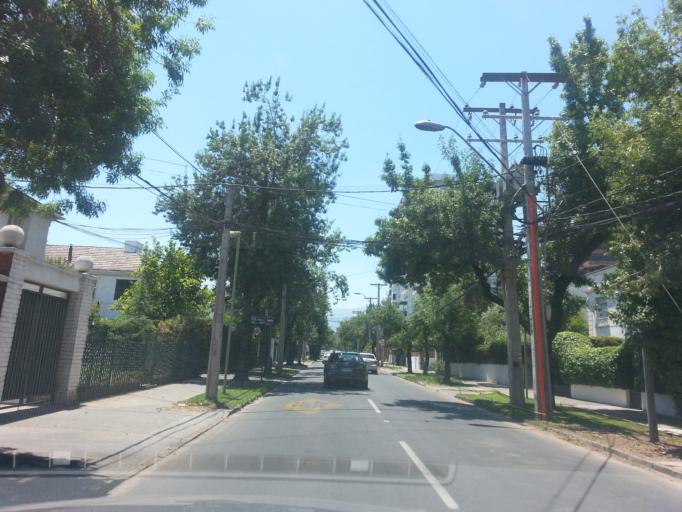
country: CL
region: Santiago Metropolitan
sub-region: Provincia de Santiago
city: Villa Presidente Frei, Nunoa, Santiago, Chile
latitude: -33.4242
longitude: -70.5911
